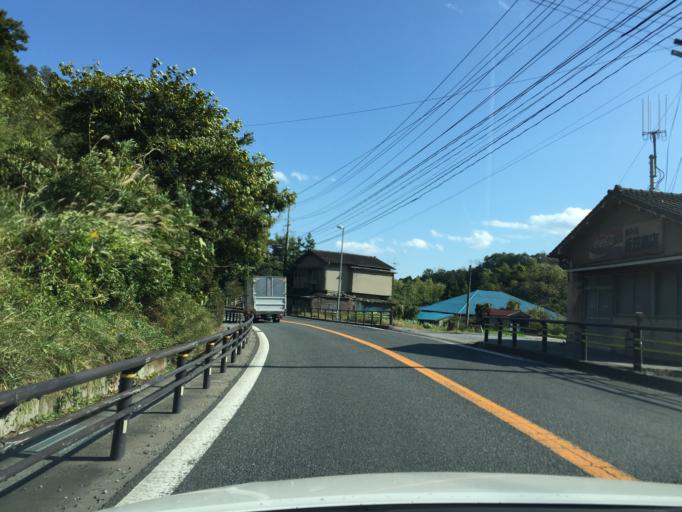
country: JP
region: Fukushima
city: Iwaki
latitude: 37.0713
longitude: 140.8295
